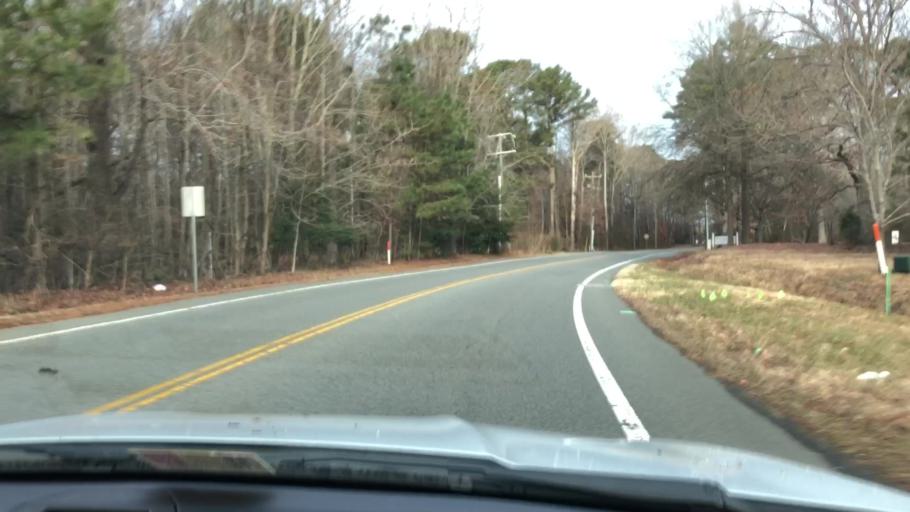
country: US
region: Virginia
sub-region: James City County
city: Williamsburg
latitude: 37.2617
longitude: -76.7390
